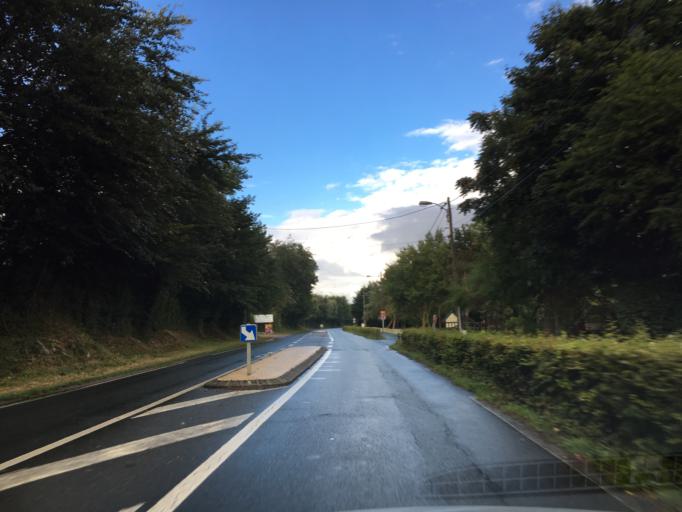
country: FR
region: Lower Normandy
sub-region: Departement du Calvados
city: Merville-Franceville-Plage
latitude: 49.2837
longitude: -0.1879
